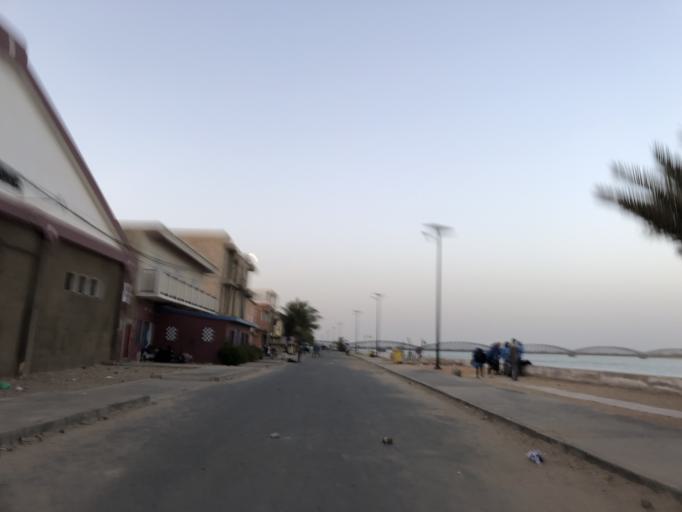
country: SN
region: Saint-Louis
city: Saint-Louis
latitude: 16.0213
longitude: -16.5043
